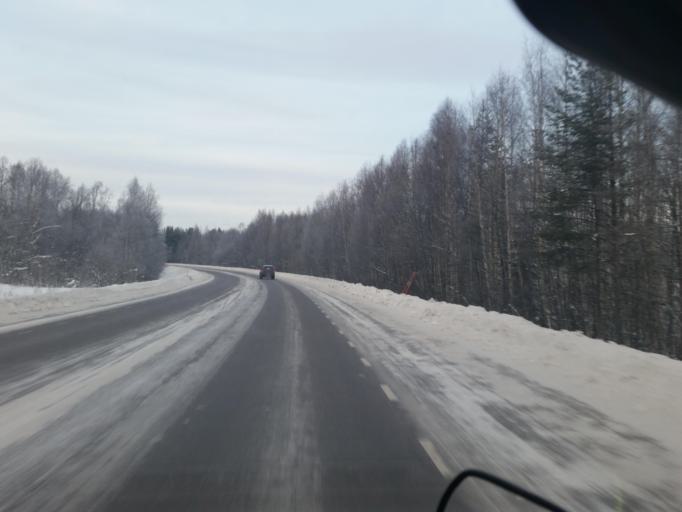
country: SE
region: Norrbotten
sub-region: Pitea Kommun
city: Pitea
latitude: 65.3038
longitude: 21.5095
